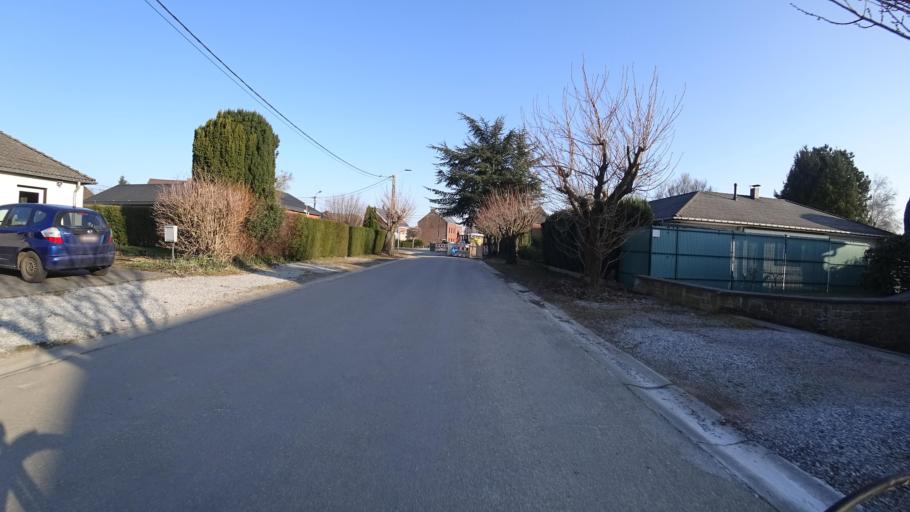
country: BE
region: Wallonia
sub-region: Province de Namur
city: Gembloux
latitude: 50.5649
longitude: 4.6780
